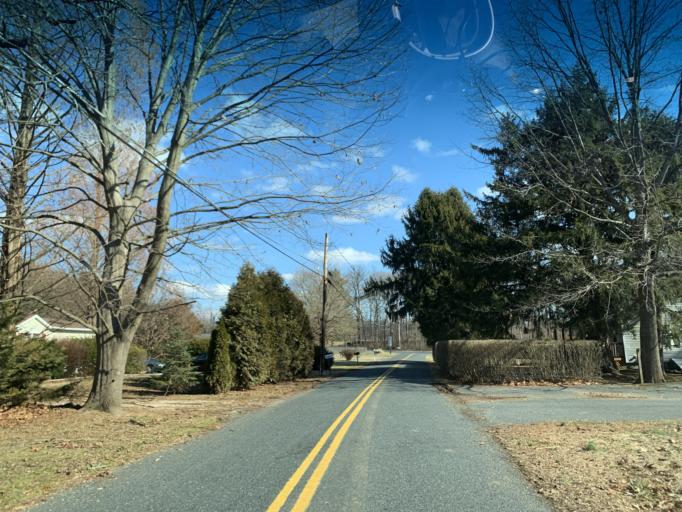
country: US
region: Maryland
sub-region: Harford County
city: Riverside
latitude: 39.5125
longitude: -76.2362
